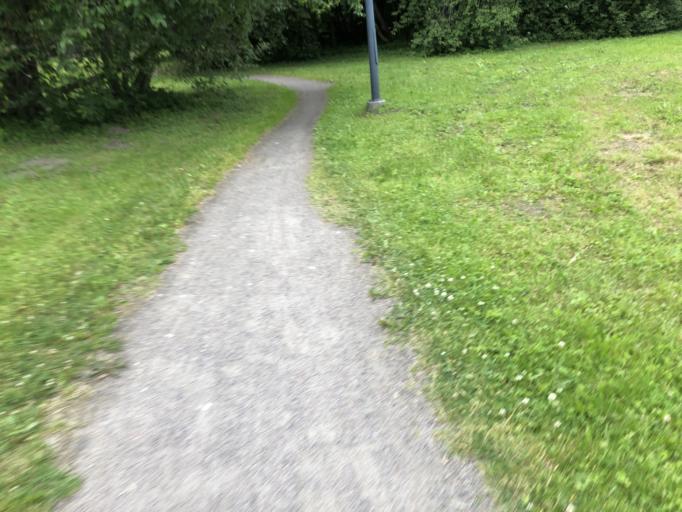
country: EE
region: Harju
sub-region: Viimsi vald
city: Viimsi
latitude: 59.4593
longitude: 24.8312
